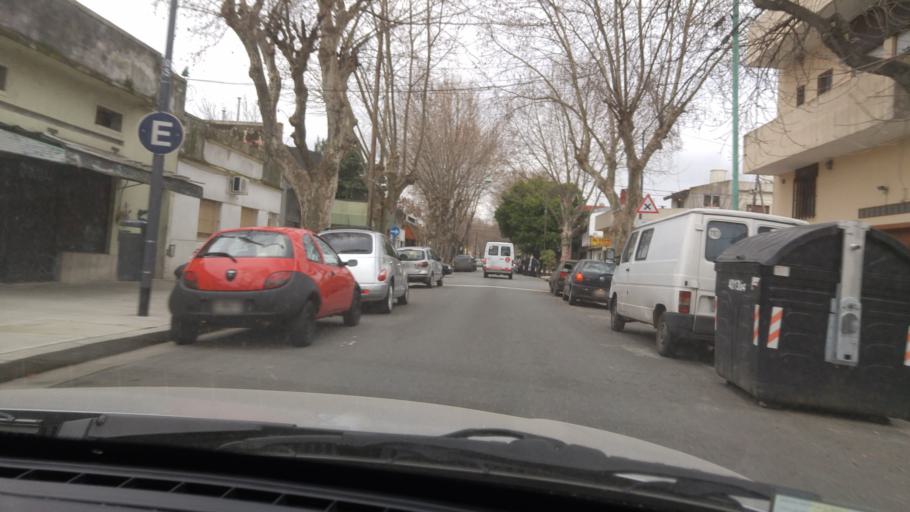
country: AR
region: Buenos Aires
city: Caseros
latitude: -34.6181
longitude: -58.5260
